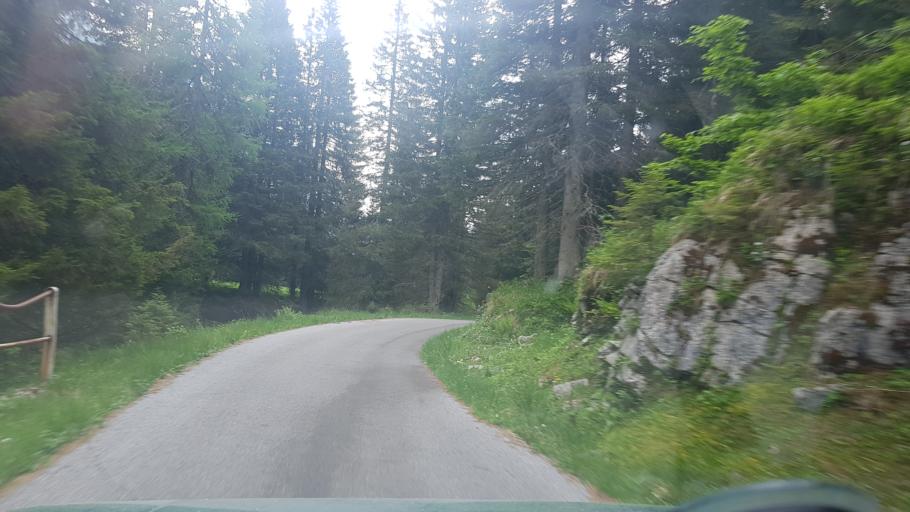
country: IT
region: Friuli Venezia Giulia
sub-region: Provincia di Udine
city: Paularo
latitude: 46.5618
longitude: 13.1776
